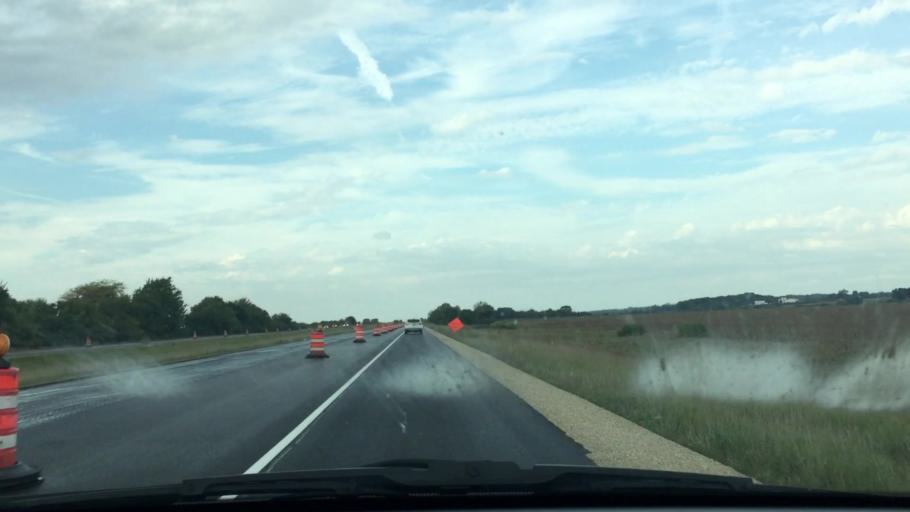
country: US
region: Illinois
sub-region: Whiteside County
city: Prophetstown
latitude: 41.7124
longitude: -90.0123
